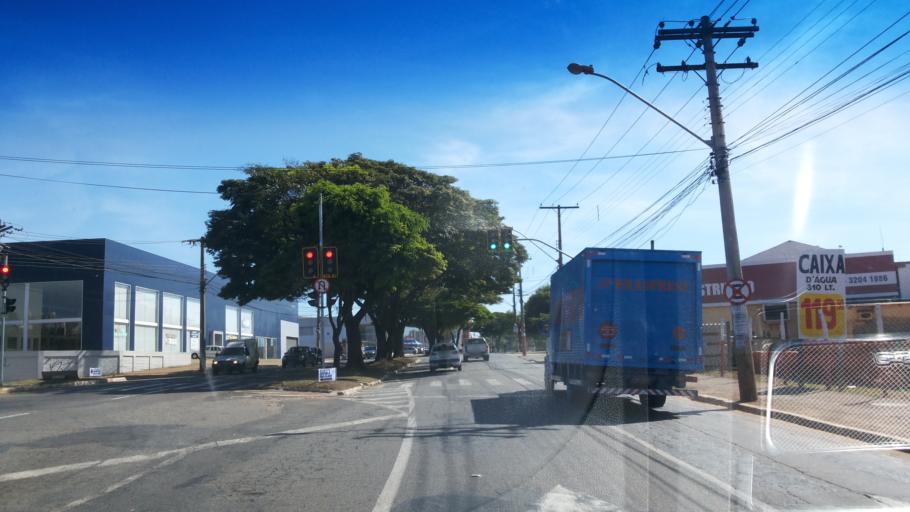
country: BR
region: Goias
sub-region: Goiania
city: Goiania
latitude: -16.6458
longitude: -49.2417
